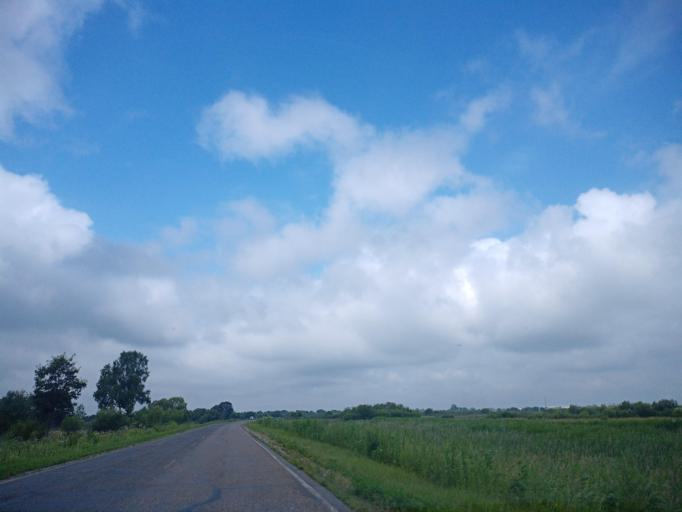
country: RU
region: Primorskiy
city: Dal'nerechensk
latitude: 45.9343
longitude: 133.8391
